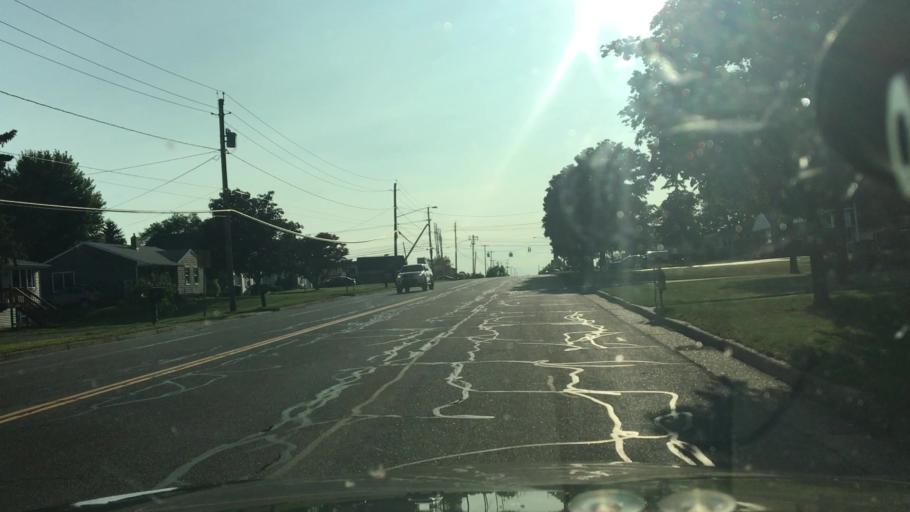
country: US
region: New York
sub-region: Erie County
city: Blasdell
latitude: 42.7969
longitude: -78.8086
